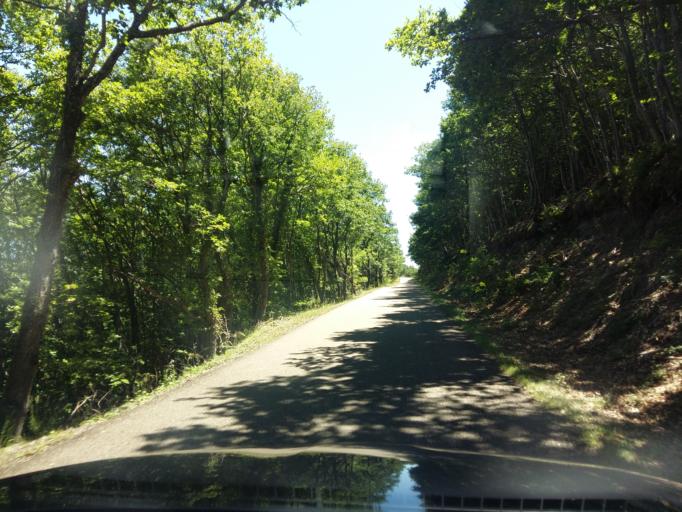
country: ES
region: Aragon
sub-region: Provincia de Zaragoza
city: Litago
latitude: 41.7955
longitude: -1.7819
